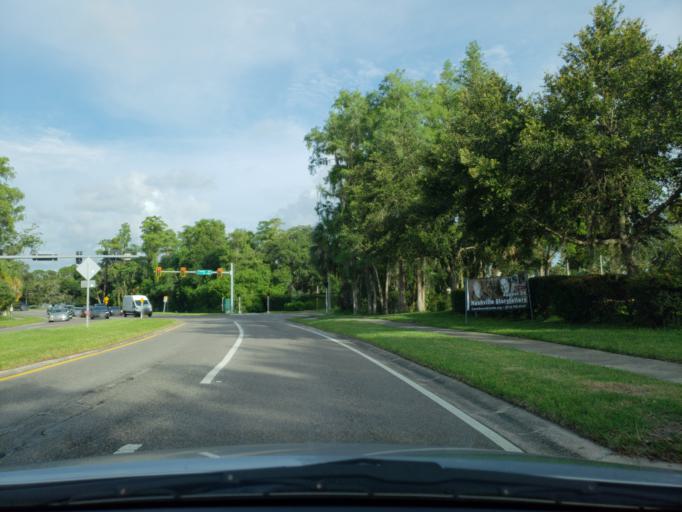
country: US
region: Florida
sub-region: Hillsborough County
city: Carrollwood Village
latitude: 28.0676
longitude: -82.5150
